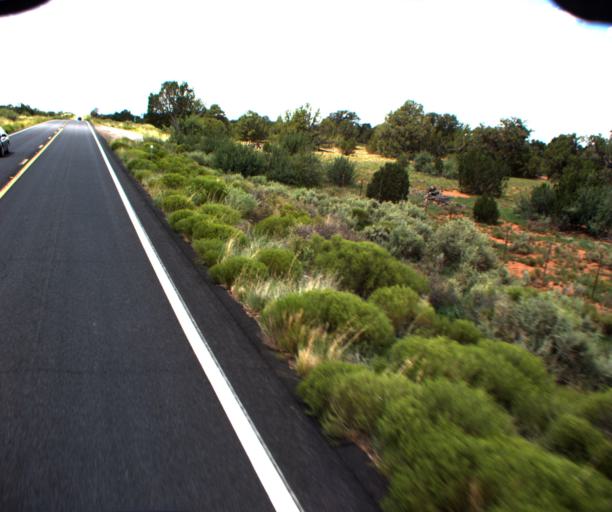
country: US
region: Arizona
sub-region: Coconino County
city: Parks
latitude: 35.6086
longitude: -112.0561
